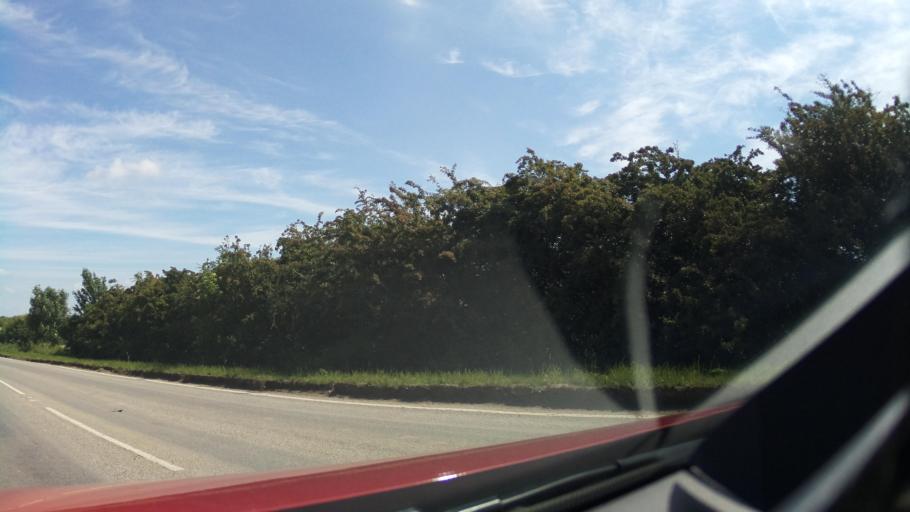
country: GB
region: England
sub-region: North Lincolnshire
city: Manton
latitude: 53.5124
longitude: -0.5810
